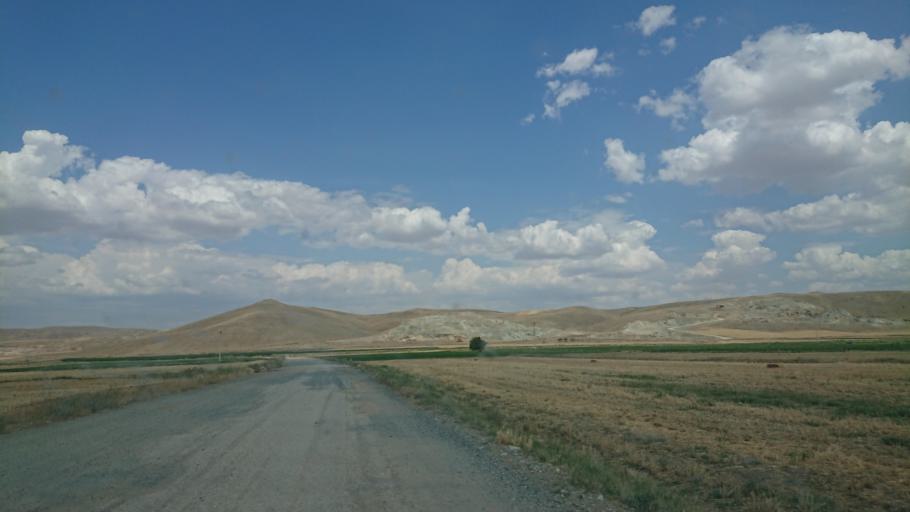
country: TR
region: Aksaray
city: Sariyahsi
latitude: 38.9809
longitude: 33.9044
